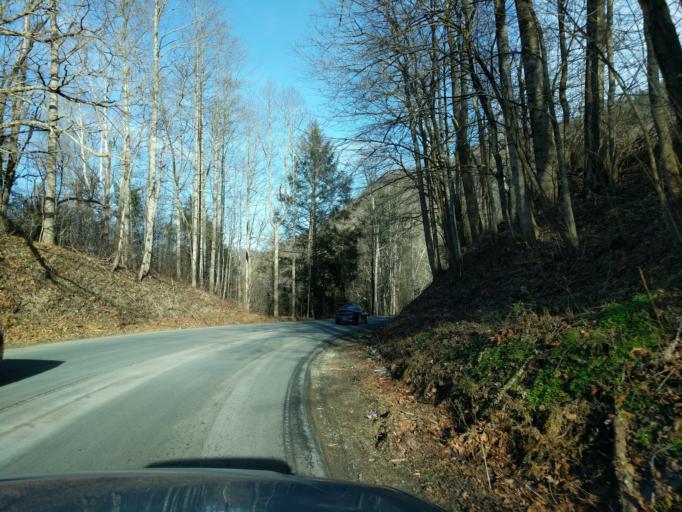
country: US
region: North Carolina
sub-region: Henderson County
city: Edneyville
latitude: 35.4150
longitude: -82.3143
